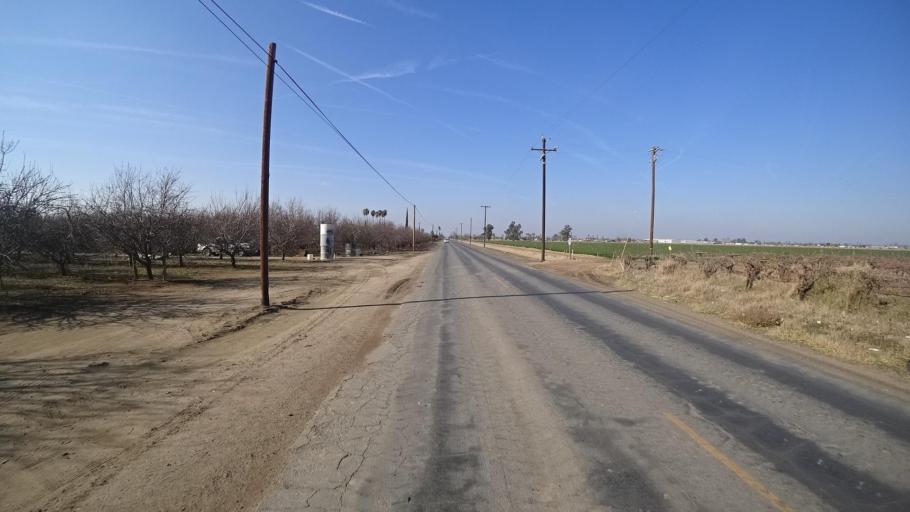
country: US
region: California
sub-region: Kern County
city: Weedpatch
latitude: 35.2379
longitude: -118.9049
